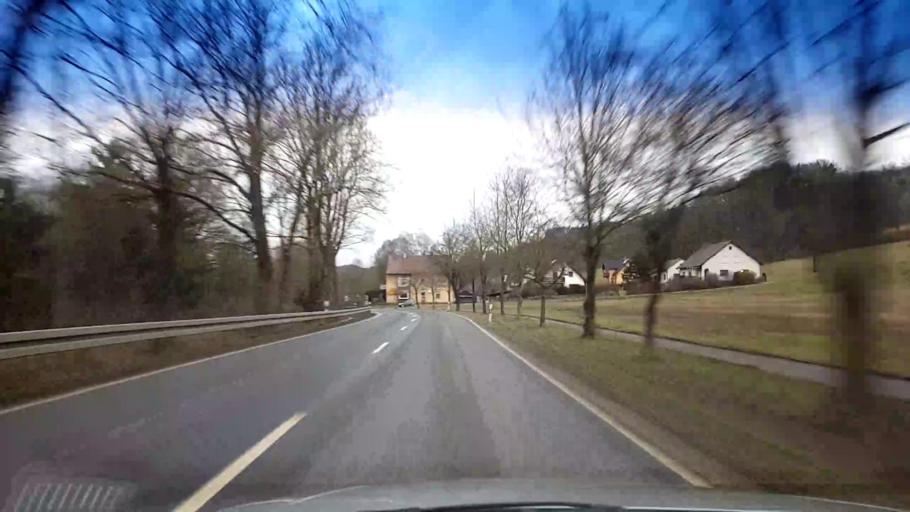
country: DE
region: Bavaria
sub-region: Upper Franconia
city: Wattendorf
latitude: 50.0673
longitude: 11.0672
